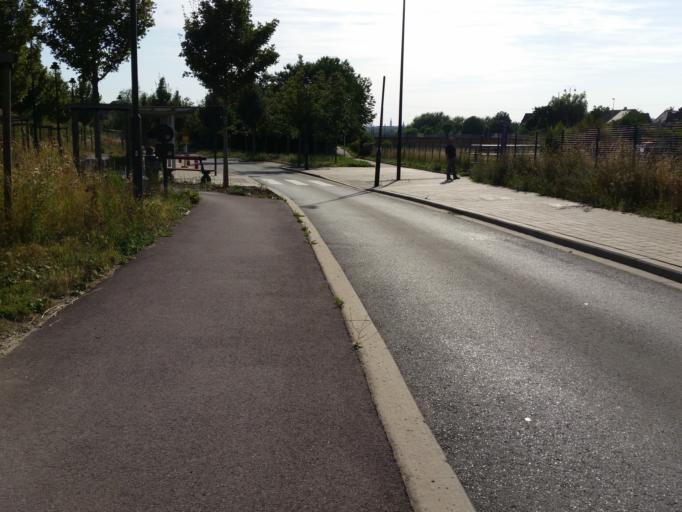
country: BE
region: Flanders
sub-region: Provincie Vlaams-Brabant
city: Diegem
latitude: 50.8898
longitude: 4.4171
